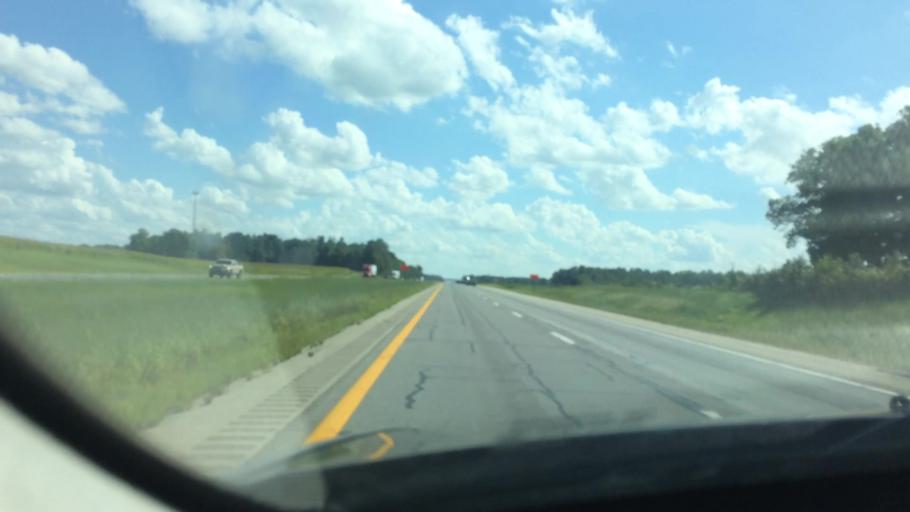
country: US
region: Ohio
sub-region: Auglaize County
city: Wapakoneta
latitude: 40.5222
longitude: -84.1696
